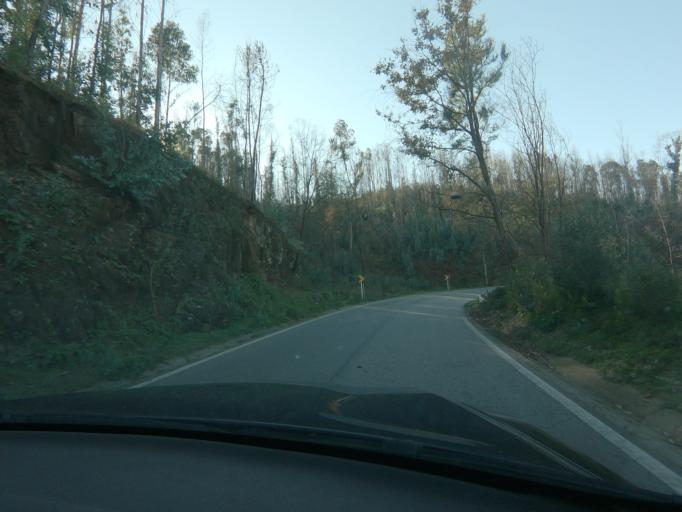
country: PT
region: Viseu
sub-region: Vouzela
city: Vouzela
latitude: 40.7295
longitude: -8.1387
